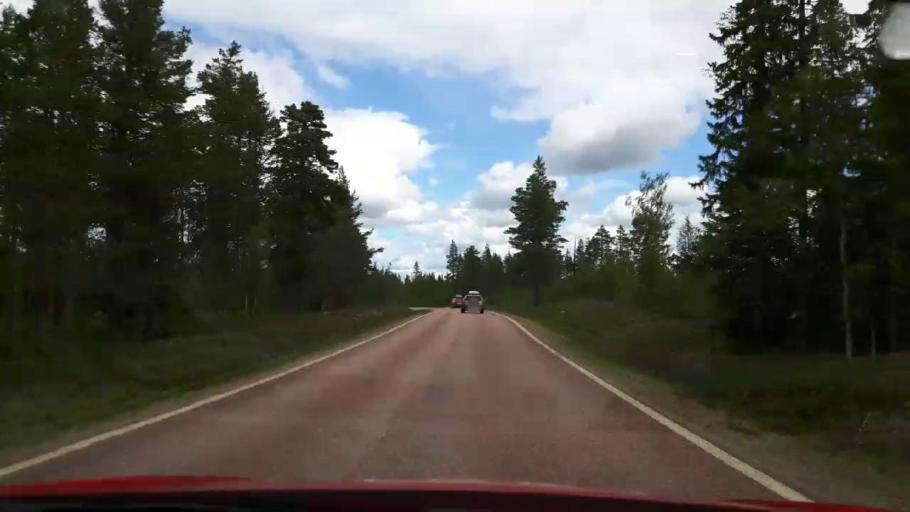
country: NO
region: Hedmark
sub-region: Trysil
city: Innbygda
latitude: 61.8748
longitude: 12.9635
